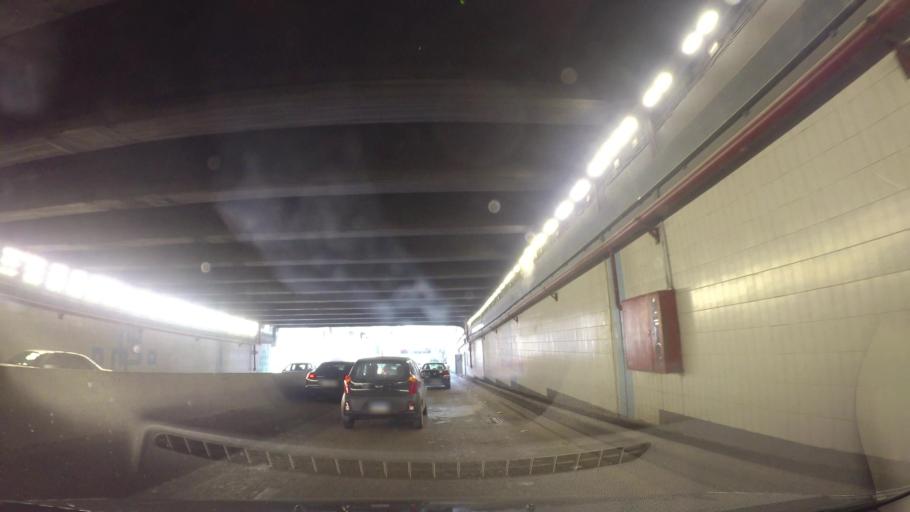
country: LB
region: Beyrouth
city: Beirut
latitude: 33.8834
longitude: 35.4970
